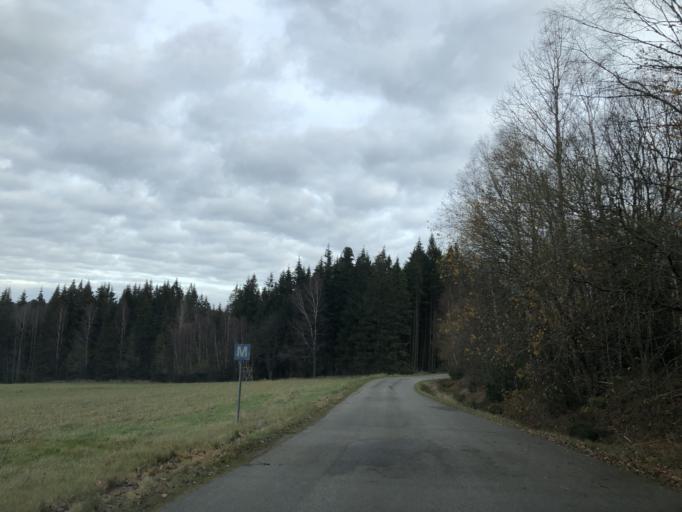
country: SE
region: Vaestra Goetaland
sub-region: Ulricehamns Kommun
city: Ulricehamn
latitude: 57.7248
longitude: 13.3591
